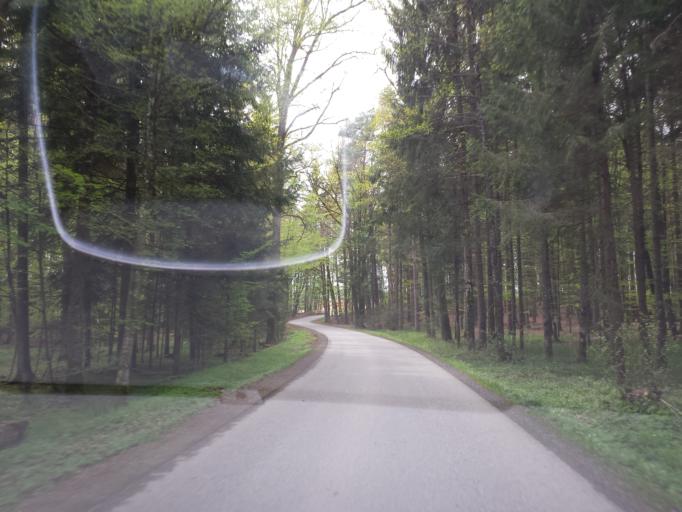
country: AT
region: Styria
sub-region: Politischer Bezirk Hartberg-Fuerstenfeld
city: Loipersdorf bei Fuerstenfeld
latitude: 47.0128
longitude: 16.1208
